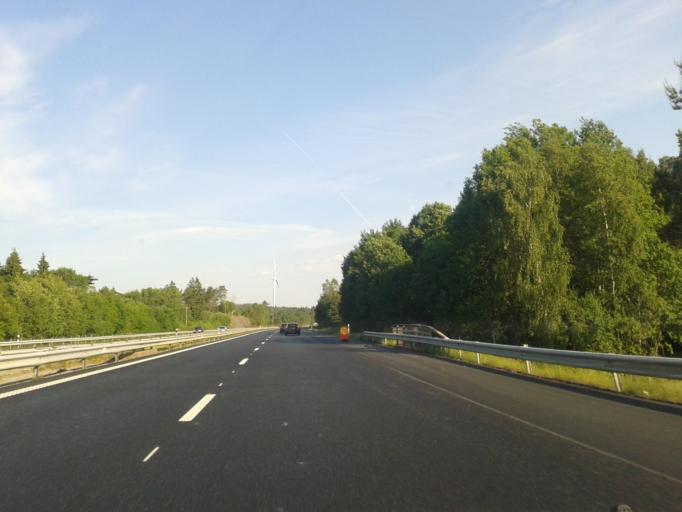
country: SE
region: Vaestra Goetaland
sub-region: Kungalvs Kommun
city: Kode
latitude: 57.9134
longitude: 11.8909
